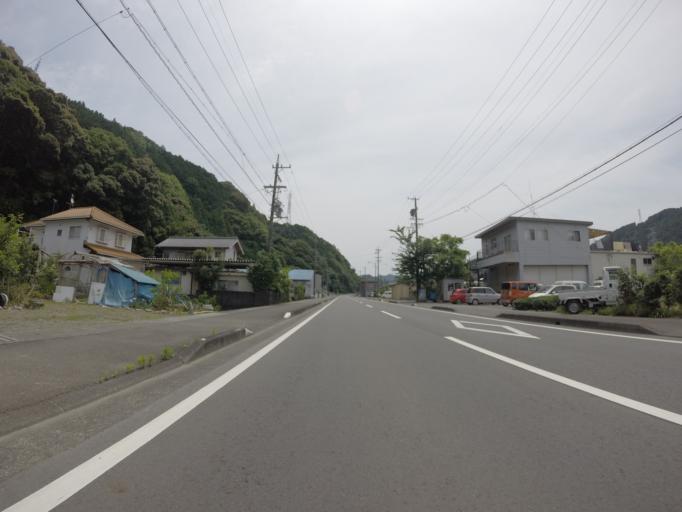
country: JP
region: Shizuoka
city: Shizuoka-shi
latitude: 34.9990
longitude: 138.2879
